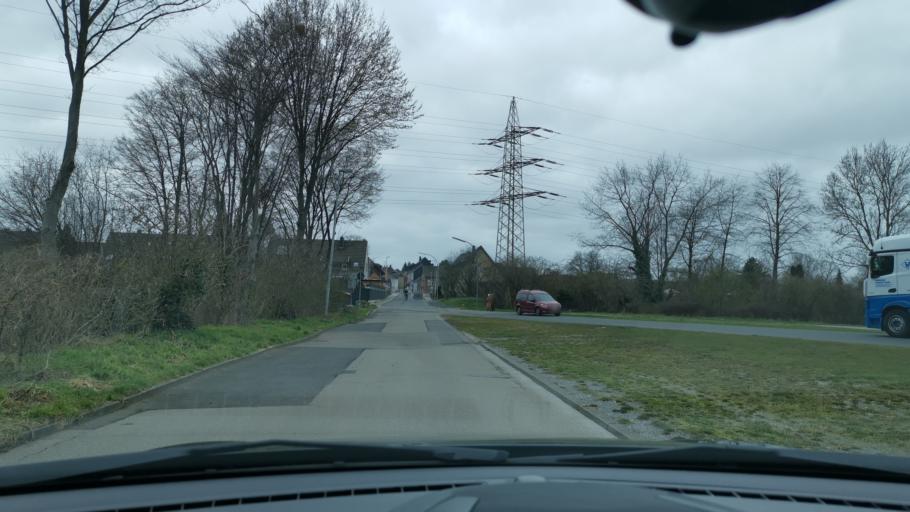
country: DE
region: North Rhine-Westphalia
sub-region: Regierungsbezirk Dusseldorf
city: Grevenbroich
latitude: 51.0705
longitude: 6.5730
